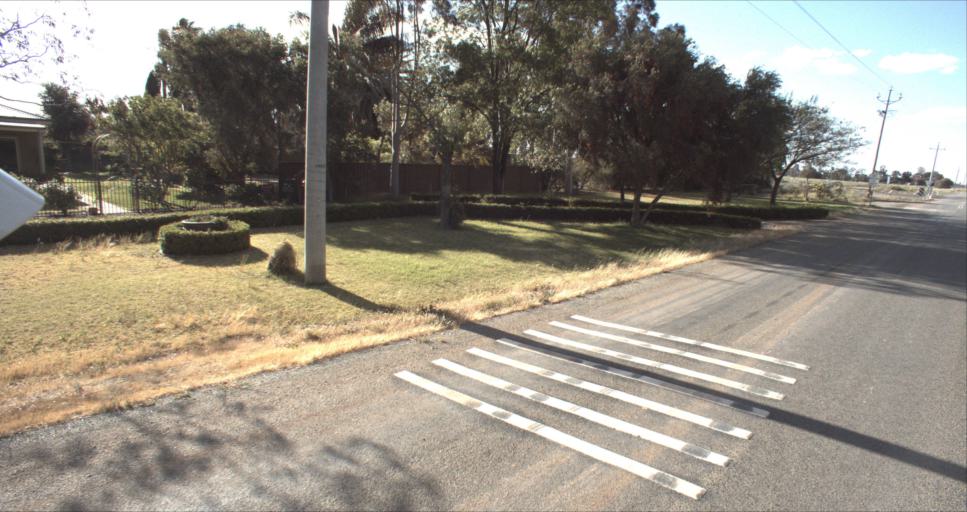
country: AU
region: New South Wales
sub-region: Leeton
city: Leeton
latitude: -34.5209
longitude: 146.2833
